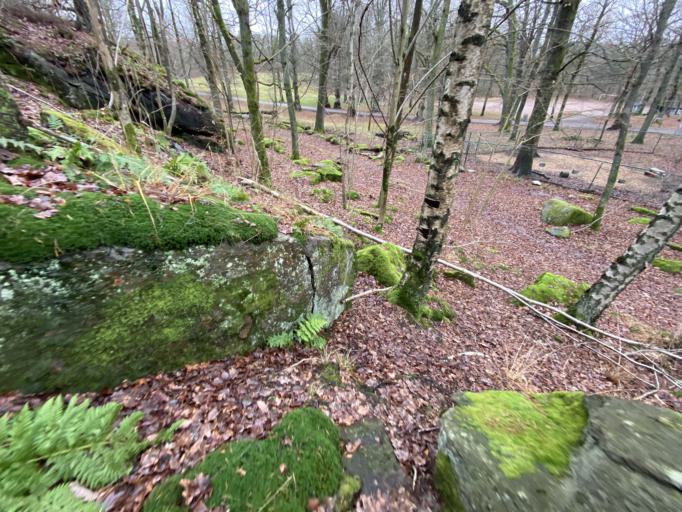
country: SE
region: Vaestra Goetaland
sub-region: Goteborg
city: Eriksbo
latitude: 57.7182
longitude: 12.0460
